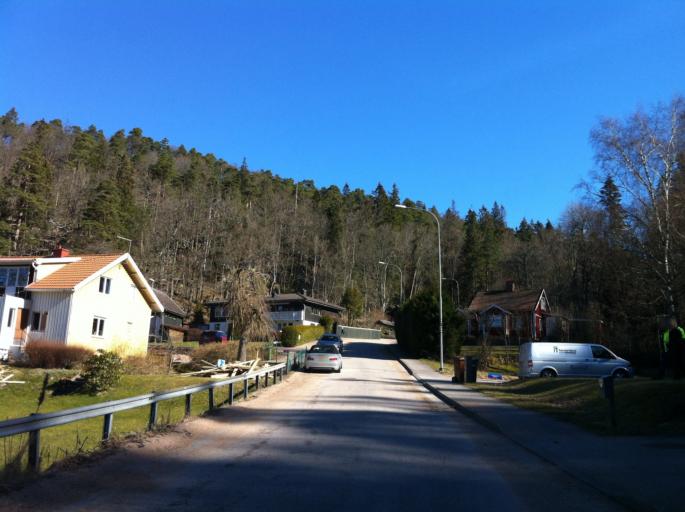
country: SE
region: Vaestra Goetaland
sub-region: Vanersborgs Kommun
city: Vargon
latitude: 58.3528
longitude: 12.4063
